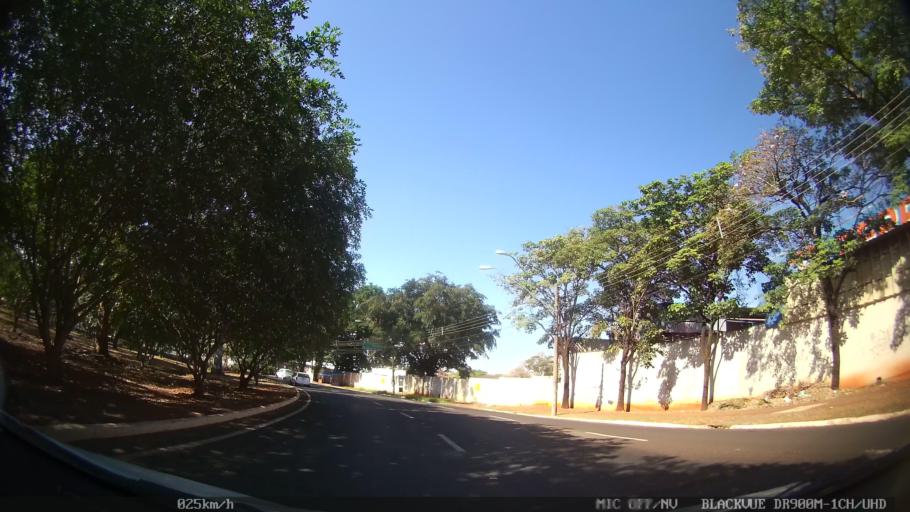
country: BR
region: Sao Paulo
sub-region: Ribeirao Preto
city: Ribeirao Preto
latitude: -21.1940
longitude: -47.7609
